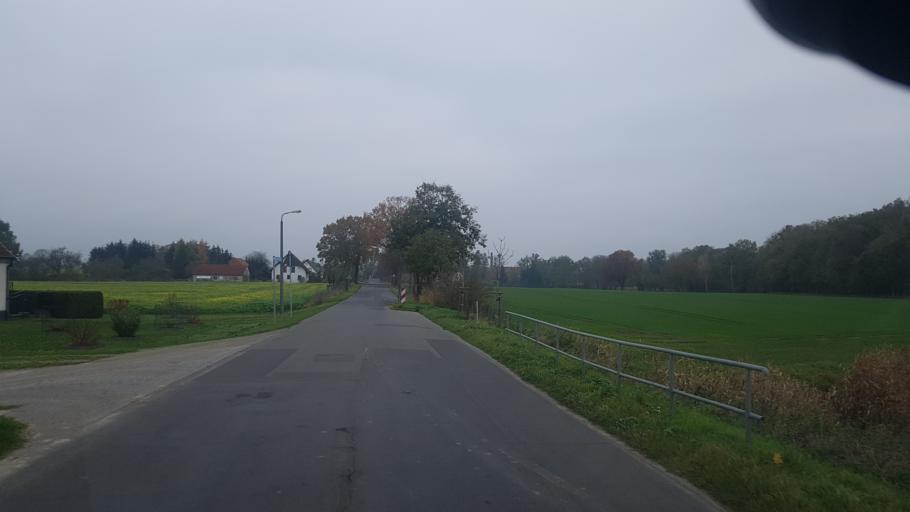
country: DE
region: Brandenburg
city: Schonermark
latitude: 52.9136
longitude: 13.1333
